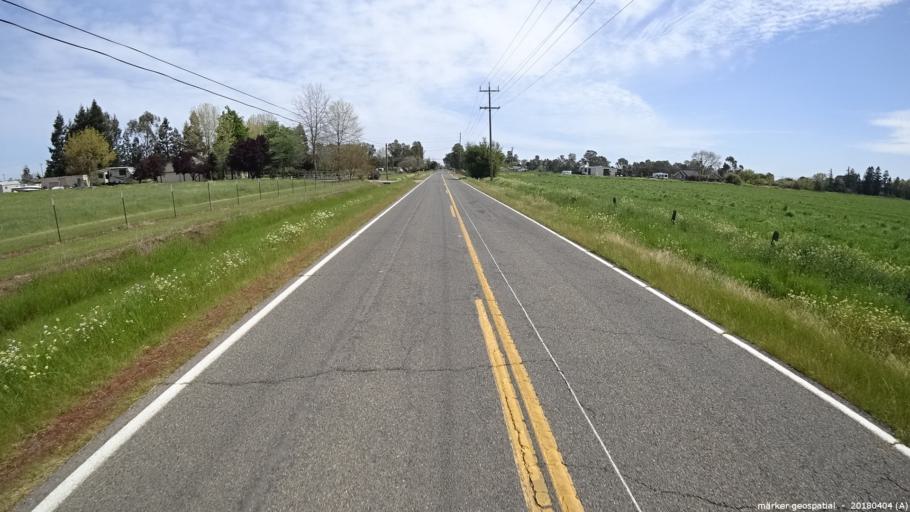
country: US
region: California
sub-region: Sacramento County
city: Galt
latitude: 38.2625
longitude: -121.2656
